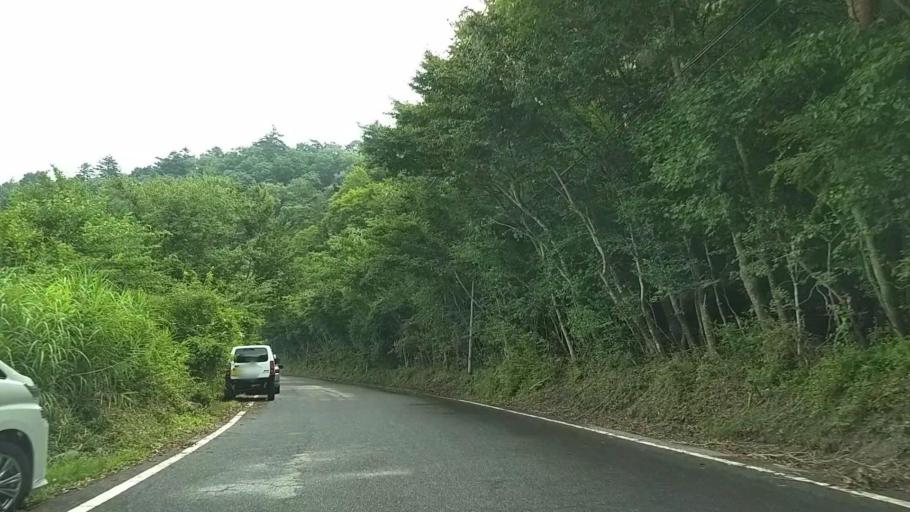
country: JP
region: Yamanashi
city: Fujikawaguchiko
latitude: 35.4680
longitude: 138.5742
